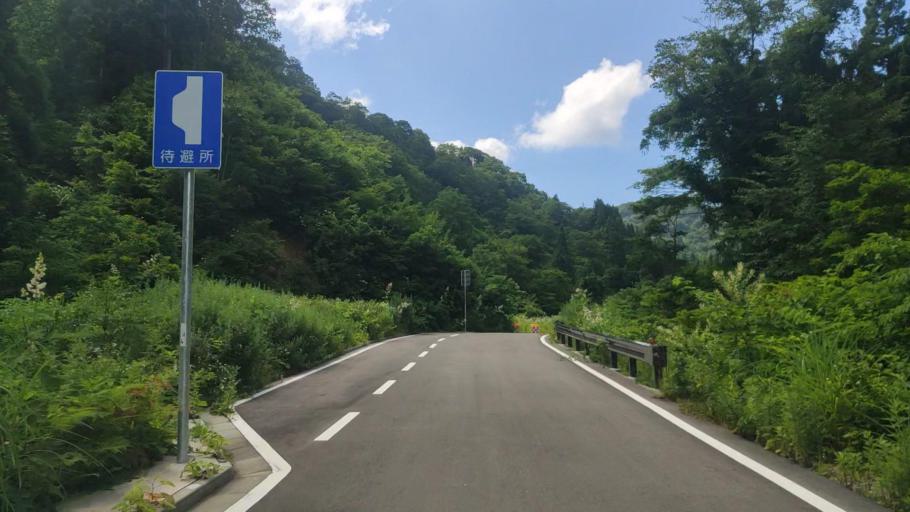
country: JP
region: Fukui
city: Katsuyama
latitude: 36.1616
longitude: 136.5266
